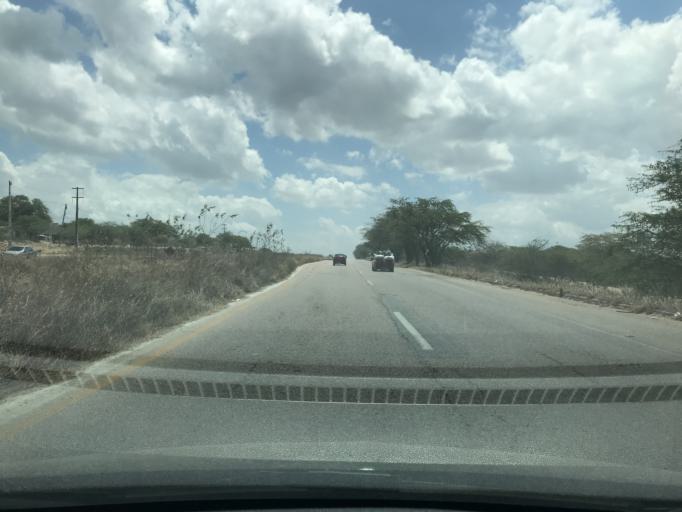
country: BR
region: Pernambuco
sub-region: Caruaru
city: Caruaru
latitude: -8.2951
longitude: -35.8882
